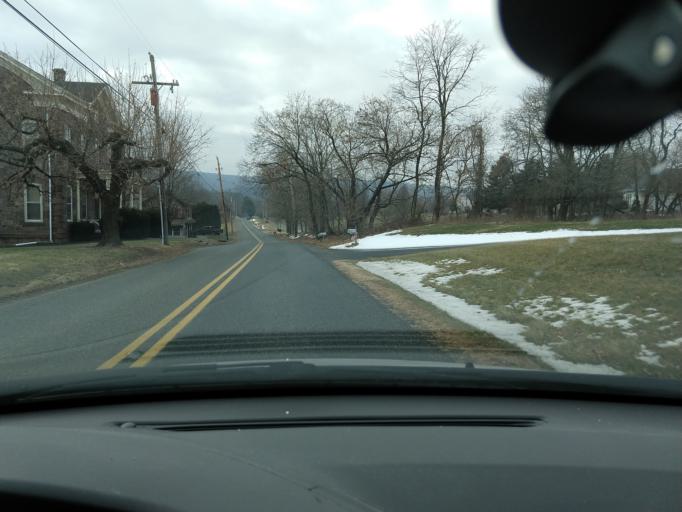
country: US
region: Pennsylvania
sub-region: Berks County
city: Amity Gardens
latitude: 40.2456
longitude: -75.7433
